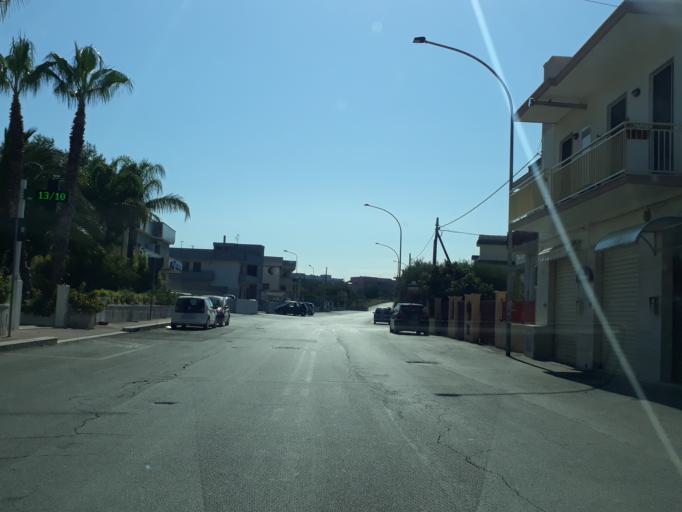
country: IT
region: Apulia
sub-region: Provincia di Bari
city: Monopoli
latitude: 40.9419
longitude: 17.3033
